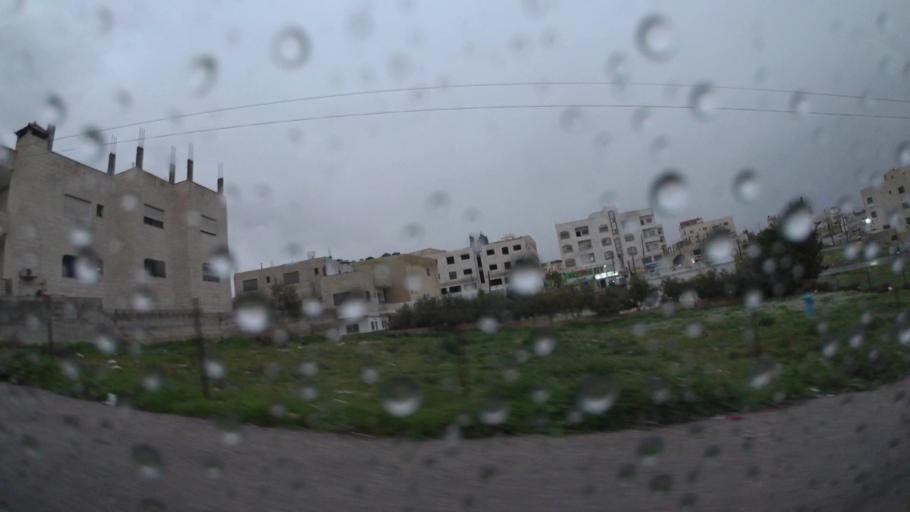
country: JO
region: Amman
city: Amman
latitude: 32.0010
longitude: 35.9580
